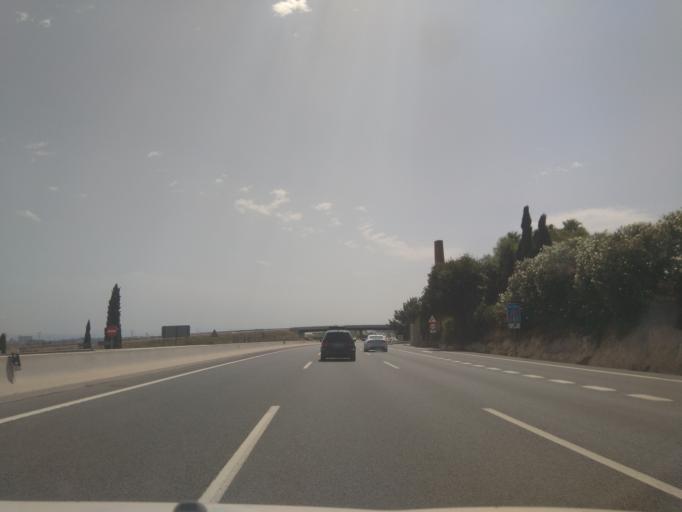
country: ES
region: Valencia
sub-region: Provincia de Valencia
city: Benifaio
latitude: 39.3138
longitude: -0.4407
